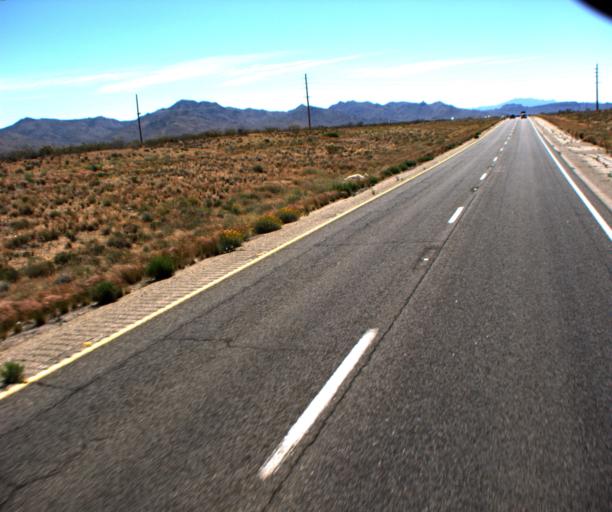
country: US
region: Arizona
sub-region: Mohave County
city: Golden Valley
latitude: 35.3213
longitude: -114.2049
